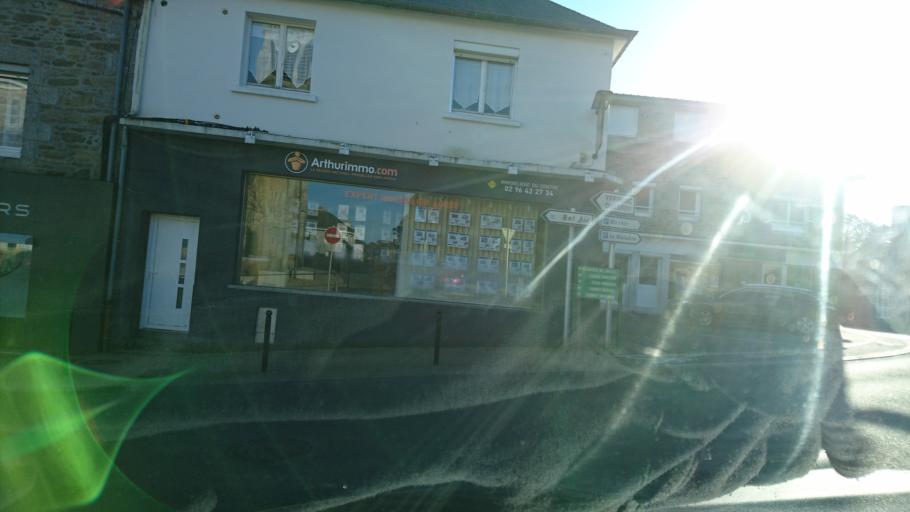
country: FR
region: Brittany
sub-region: Departement des Cotes-d'Armor
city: Pledran
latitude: 48.4450
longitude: -2.7458
